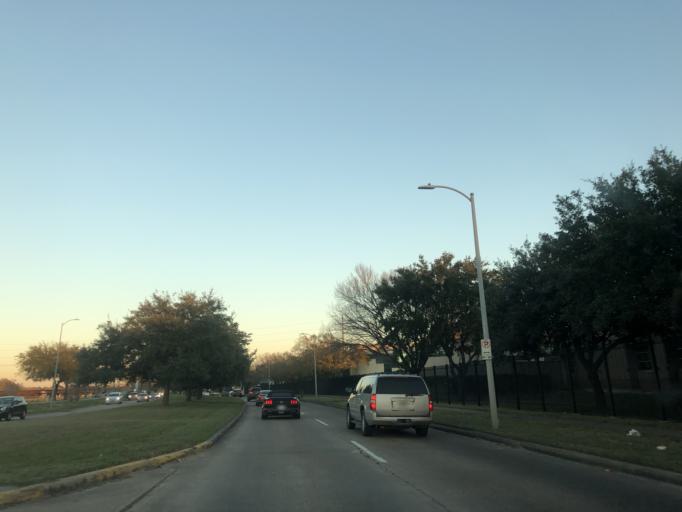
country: US
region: Texas
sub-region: Harris County
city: Bellaire
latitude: 29.6746
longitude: -95.4850
